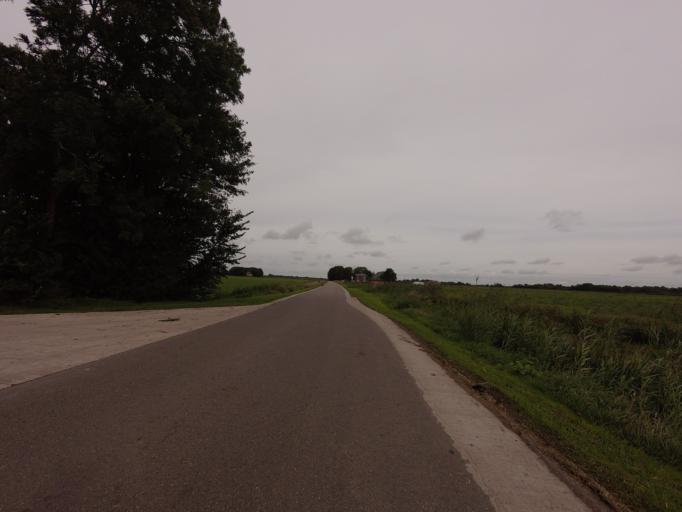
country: NL
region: Overijssel
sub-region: Gemeente Steenwijkerland
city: Blokzijl
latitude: 52.7424
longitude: 5.9661
